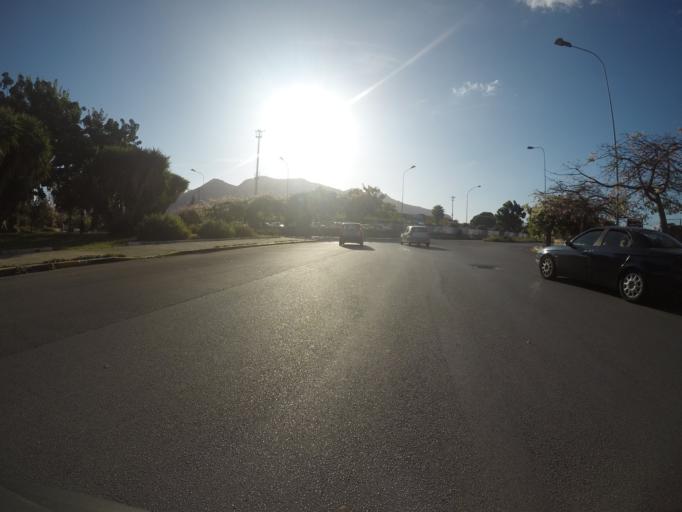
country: IT
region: Sicily
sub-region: Palermo
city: Palermo
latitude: 38.1888
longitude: 13.3147
